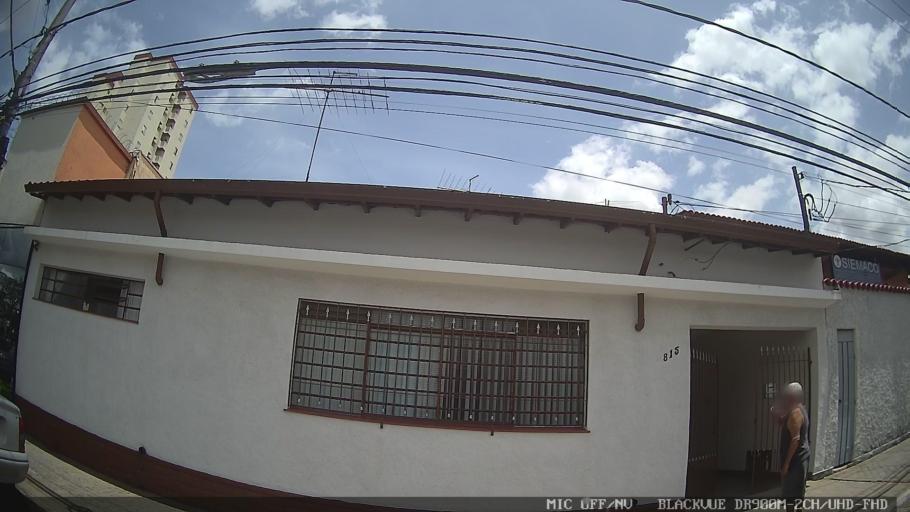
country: BR
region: Sao Paulo
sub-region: Mogi das Cruzes
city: Mogi das Cruzes
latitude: -23.5321
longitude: -46.2052
